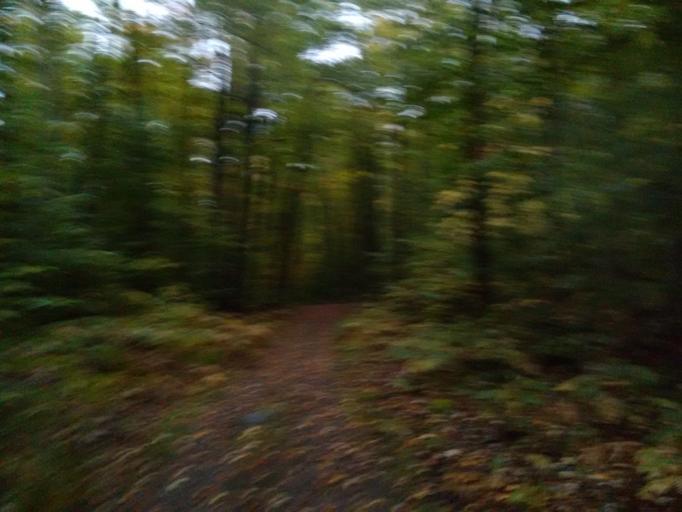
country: CA
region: Quebec
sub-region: Outaouais
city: Wakefield
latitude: 45.5329
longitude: -75.9014
